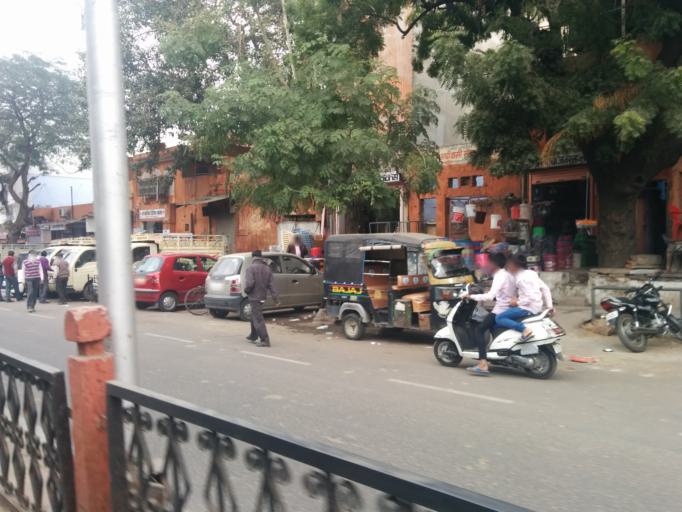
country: IN
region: Rajasthan
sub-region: Jaipur
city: Jaipur
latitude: 26.9267
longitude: 75.8190
